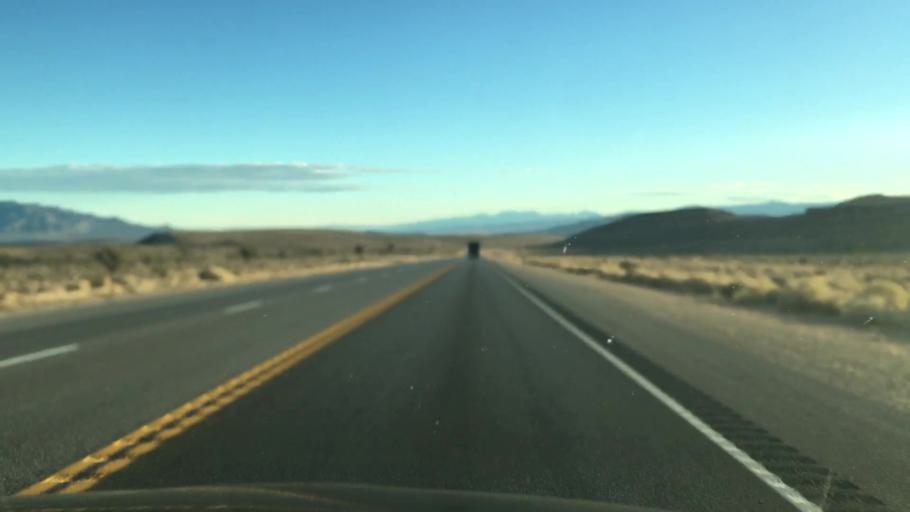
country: US
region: Nevada
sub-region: Esmeralda County
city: Goldfield
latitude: 37.6646
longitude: -117.2182
